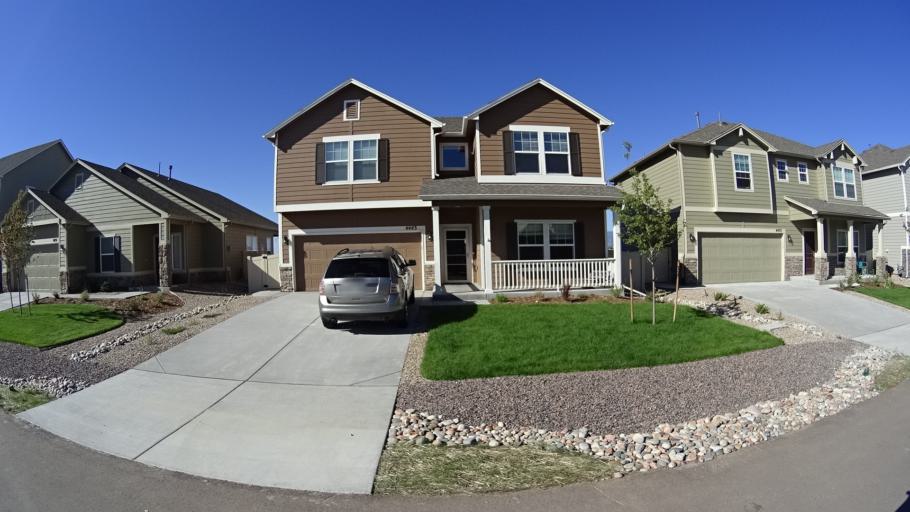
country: US
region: Colorado
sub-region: El Paso County
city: Cimarron Hills
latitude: 38.8950
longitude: -104.6745
